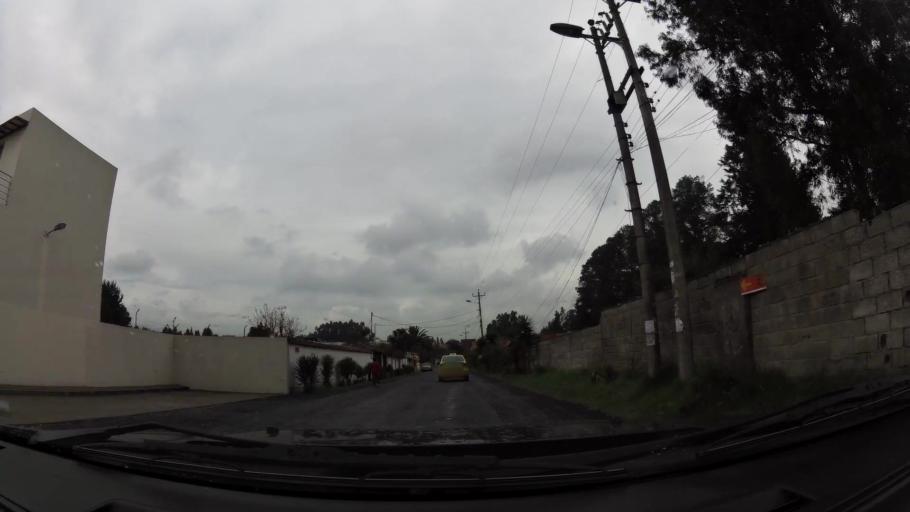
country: EC
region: Pichincha
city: Sangolqui
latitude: -0.2927
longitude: -78.4484
